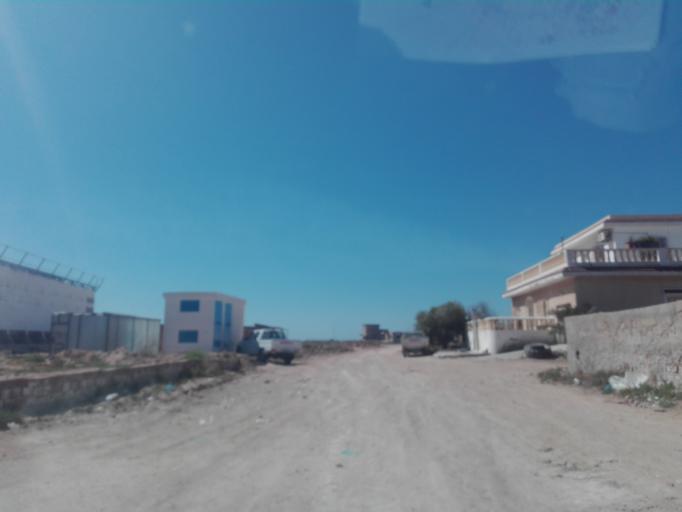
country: TN
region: Safaqis
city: Al Qarmadah
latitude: 34.7043
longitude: 11.1980
